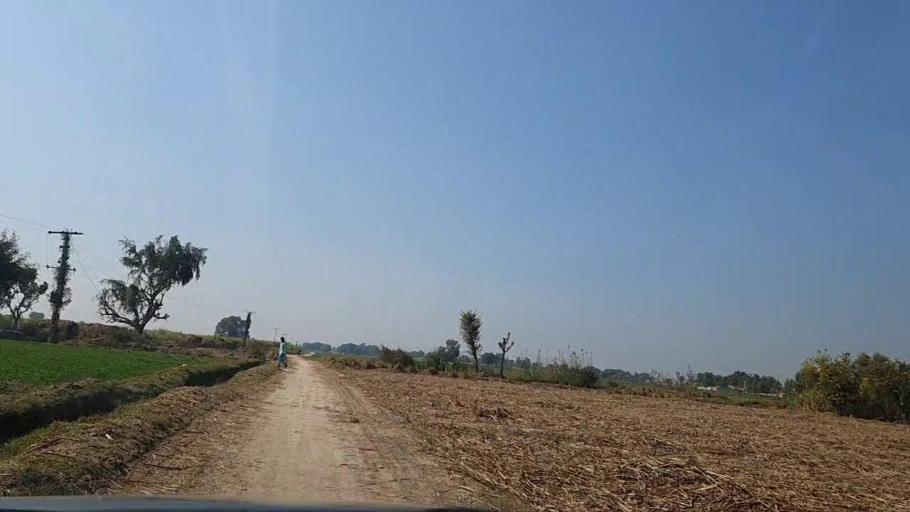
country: PK
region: Sindh
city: Daulatpur
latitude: 26.2890
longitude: 68.0625
